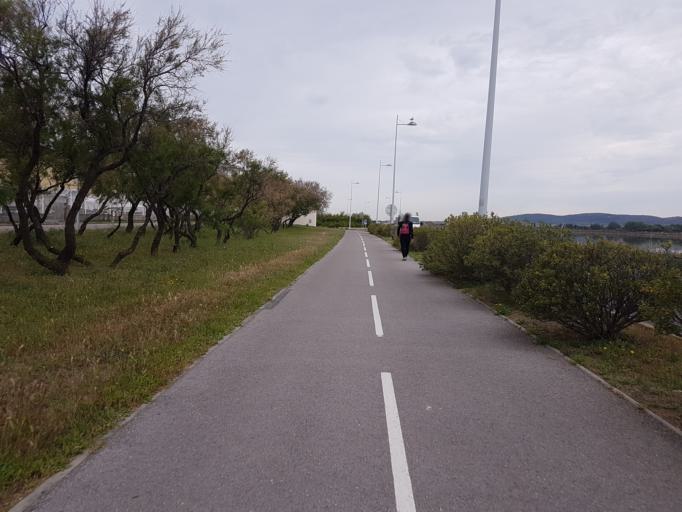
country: FR
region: Languedoc-Roussillon
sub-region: Departement de l'Herault
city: Frontignan
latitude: 43.4354
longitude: 3.7730
